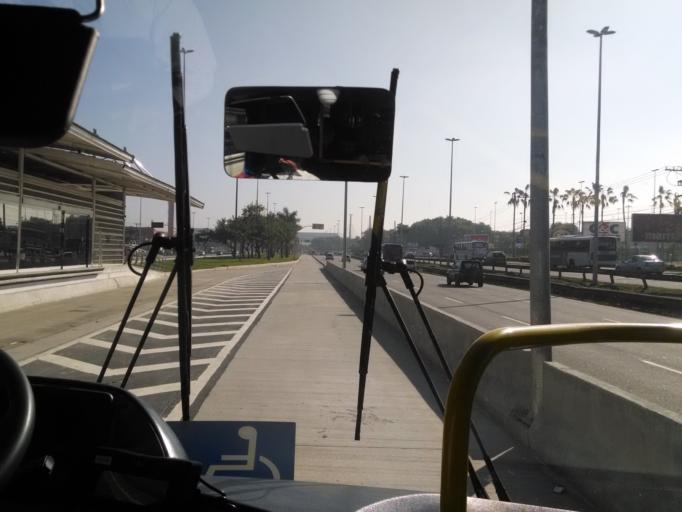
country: BR
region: Rio de Janeiro
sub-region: Rio De Janeiro
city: Rio de Janeiro
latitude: -22.9839
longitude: -43.3655
